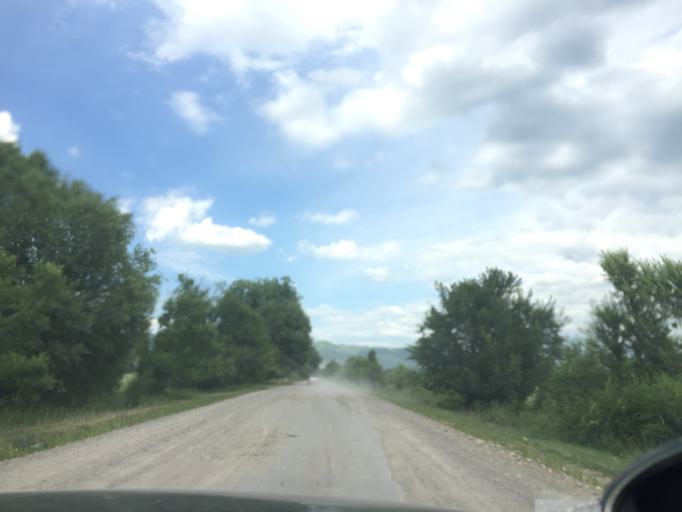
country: KG
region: Ysyk-Koel
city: Teploklyuchenka
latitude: 42.6427
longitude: 78.7875
